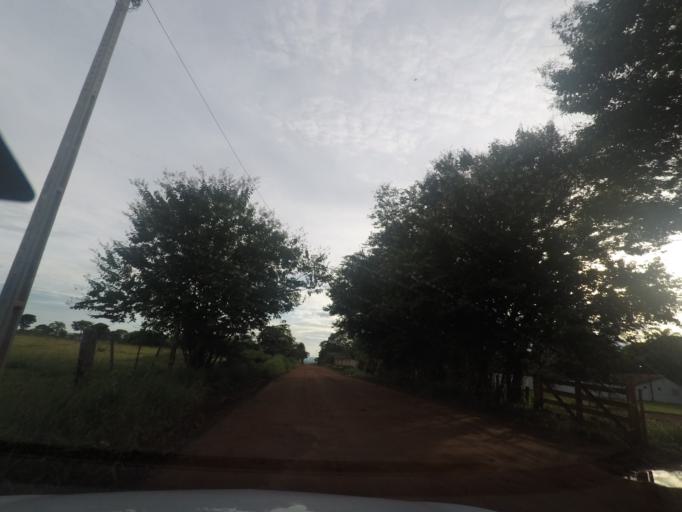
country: BR
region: Goias
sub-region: Trindade
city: Trindade
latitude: -16.7339
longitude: -49.4161
